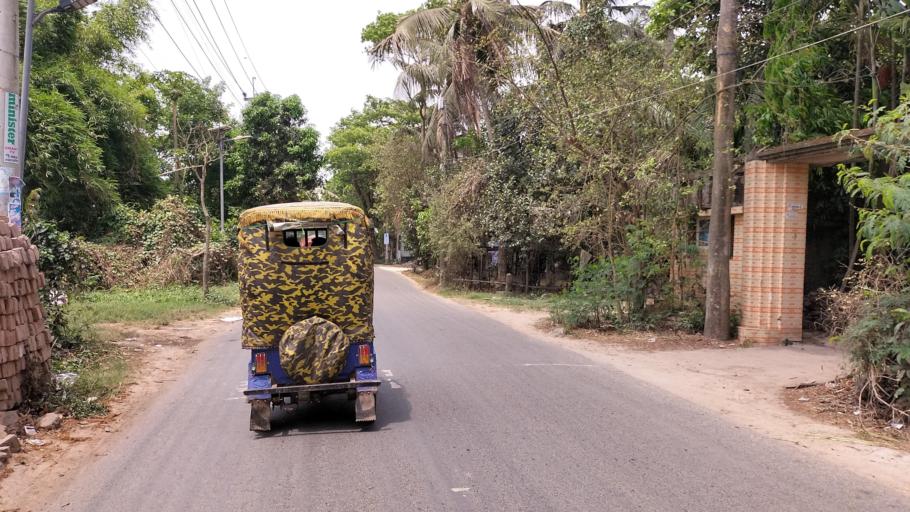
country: BD
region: Dhaka
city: Azimpur
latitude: 23.7313
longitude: 90.3088
